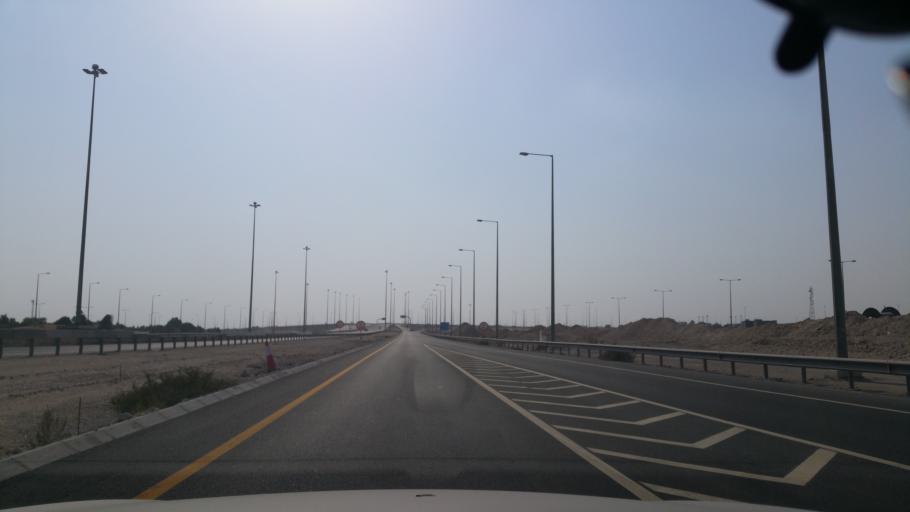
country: QA
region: Baladiyat Umm Salal
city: Umm Salal `Ali
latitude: 25.4511
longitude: 51.4192
